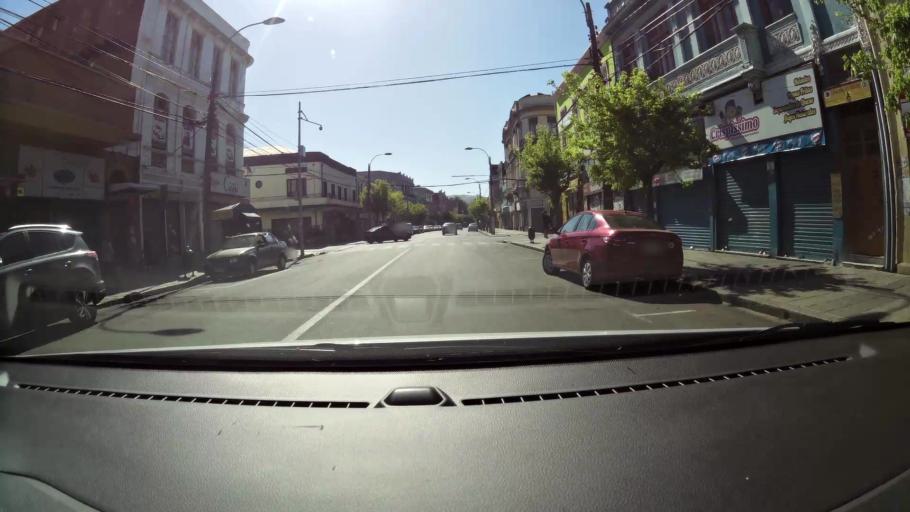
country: CL
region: Valparaiso
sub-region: Provincia de Valparaiso
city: Valparaiso
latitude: -33.0484
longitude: -71.6108
